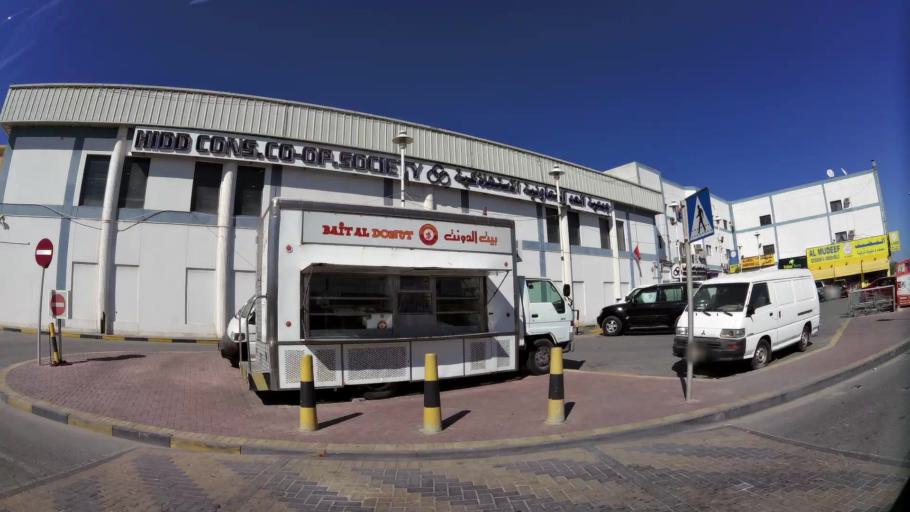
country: BH
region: Muharraq
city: Al Hadd
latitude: 26.2415
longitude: 50.6564
